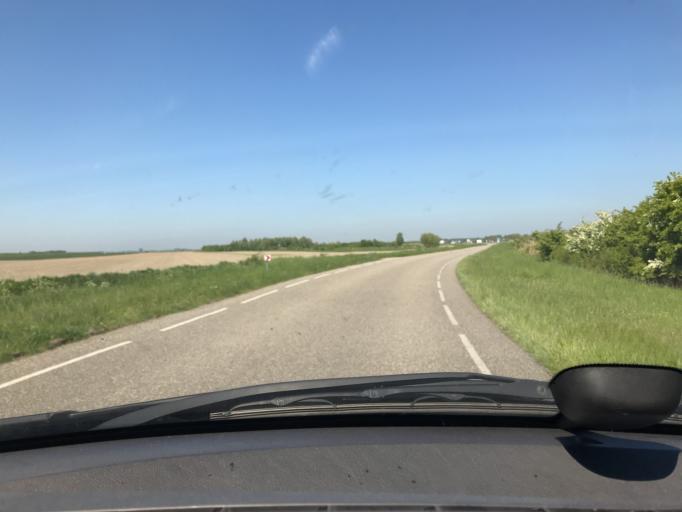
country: NL
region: Zeeland
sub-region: Gemeente Noord-Beveland
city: Kamperland
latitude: 51.5389
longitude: 3.7899
